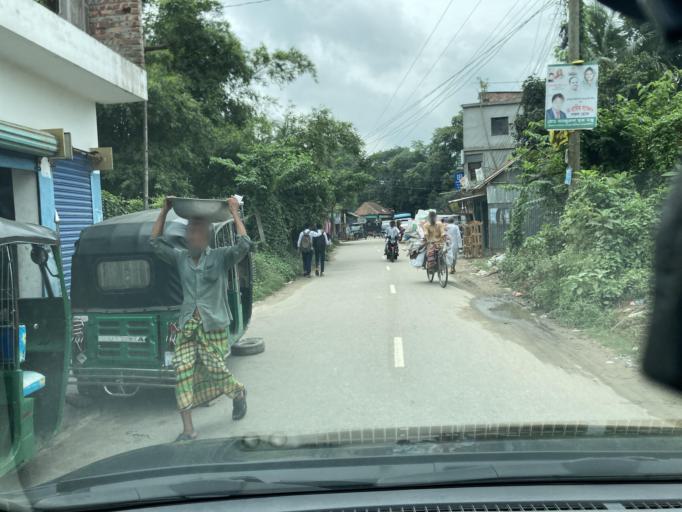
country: BD
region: Dhaka
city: Dohar
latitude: 23.7627
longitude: 90.1920
